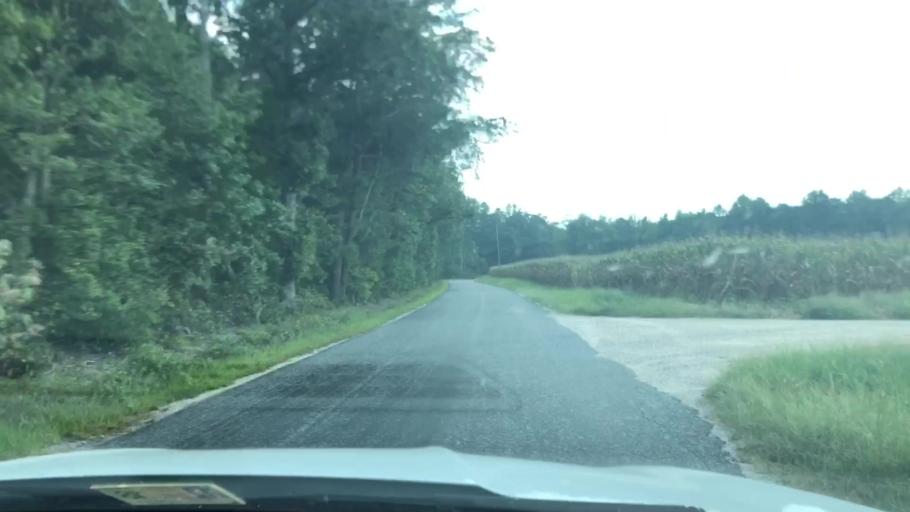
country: US
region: Virginia
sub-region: Middlesex County
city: Saluda
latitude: 37.6696
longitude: -76.6830
